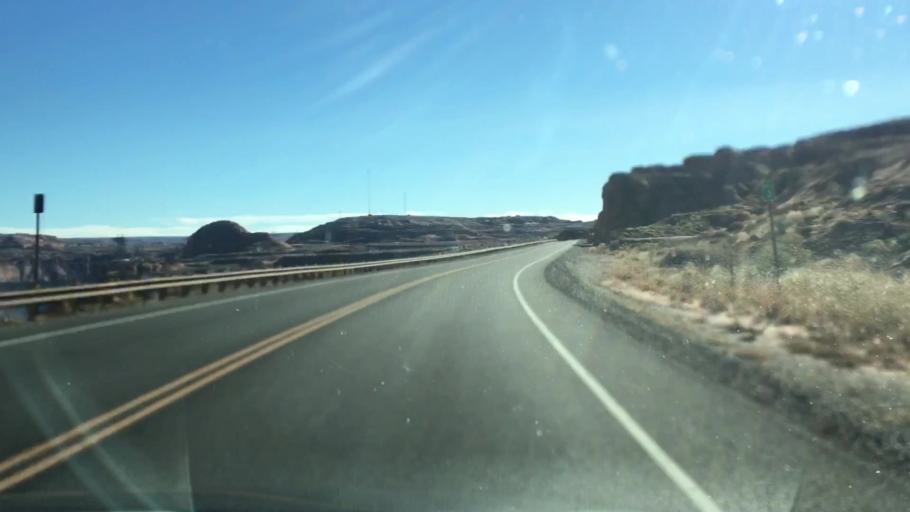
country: US
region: Arizona
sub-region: Coconino County
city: Page
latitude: 36.9542
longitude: -111.4927
